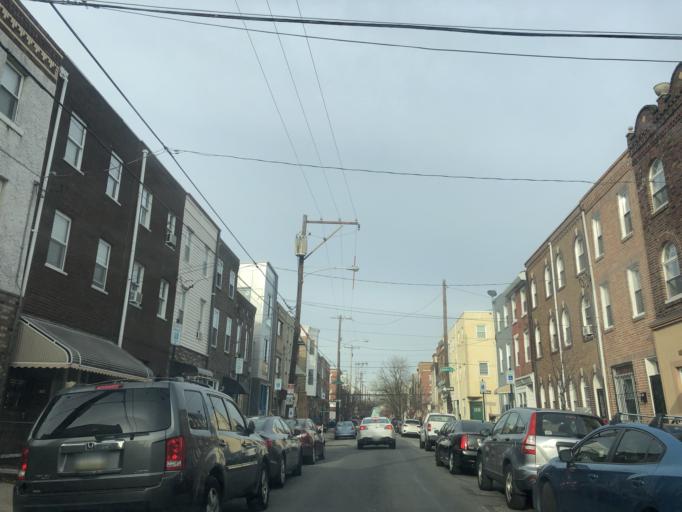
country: US
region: Pennsylvania
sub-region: Philadelphia County
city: Philadelphia
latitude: 39.9318
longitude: -75.1562
